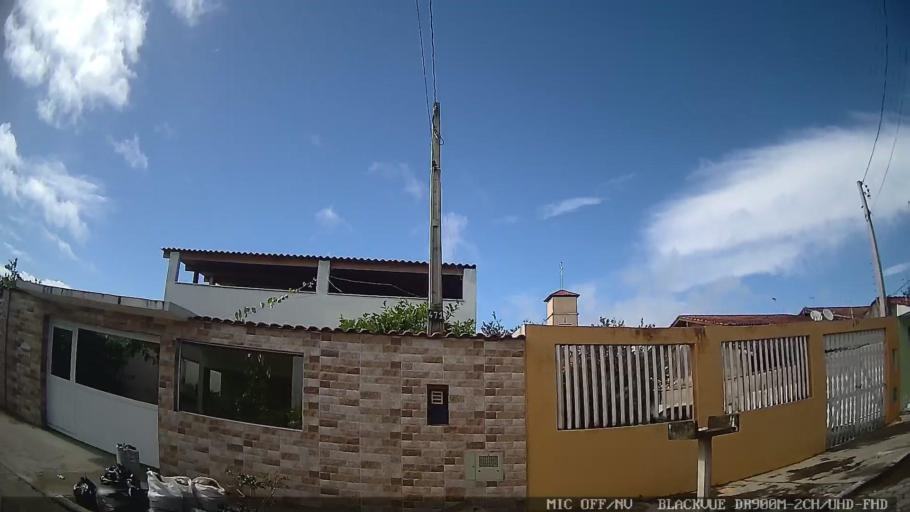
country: BR
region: Sao Paulo
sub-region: Itanhaem
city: Itanhaem
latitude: -24.2438
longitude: -46.8905
